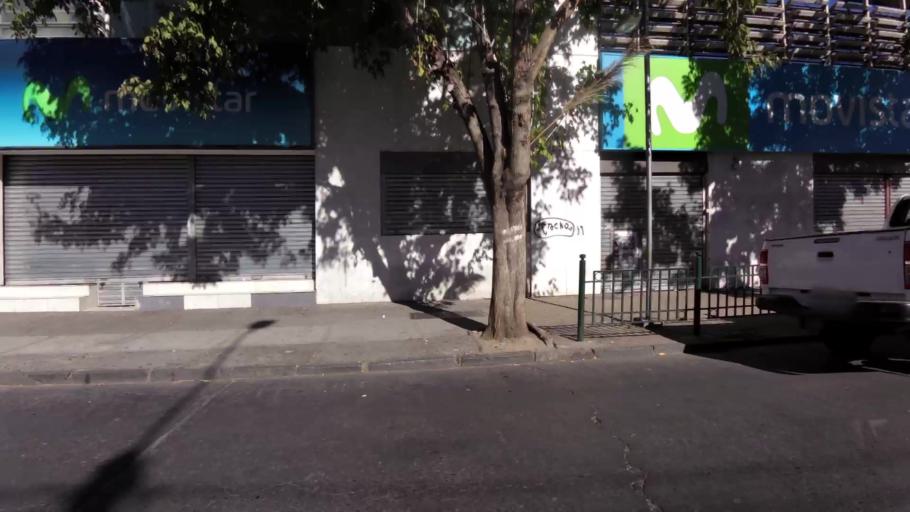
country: CL
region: O'Higgins
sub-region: Provincia de Cachapoal
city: Rancagua
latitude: -34.1701
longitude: -70.7464
